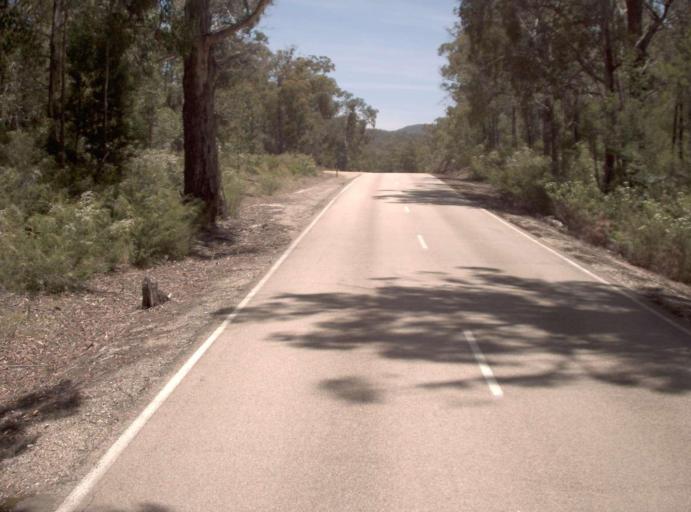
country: AU
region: Victoria
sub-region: East Gippsland
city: Lakes Entrance
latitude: -37.6515
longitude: 147.8882
